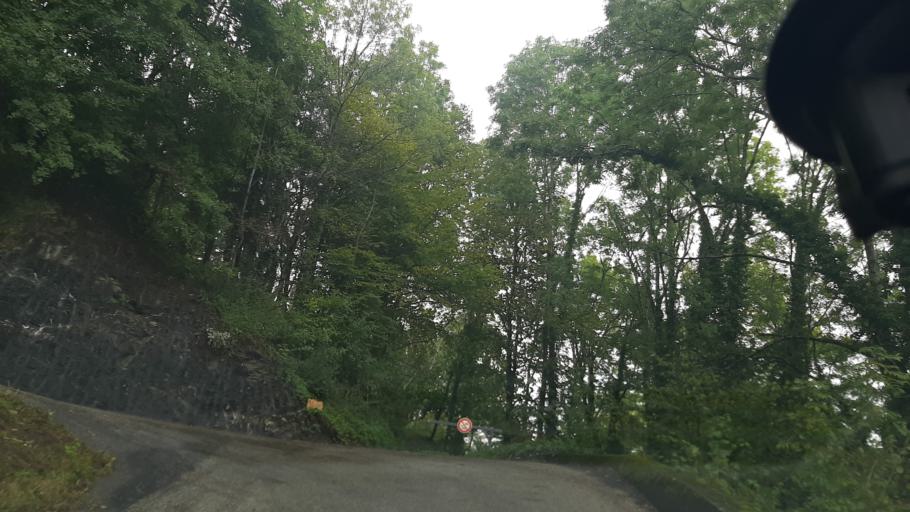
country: FR
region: Rhone-Alpes
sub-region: Departement de la Savoie
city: Gresy-sur-Isere
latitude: 45.6215
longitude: 6.2769
